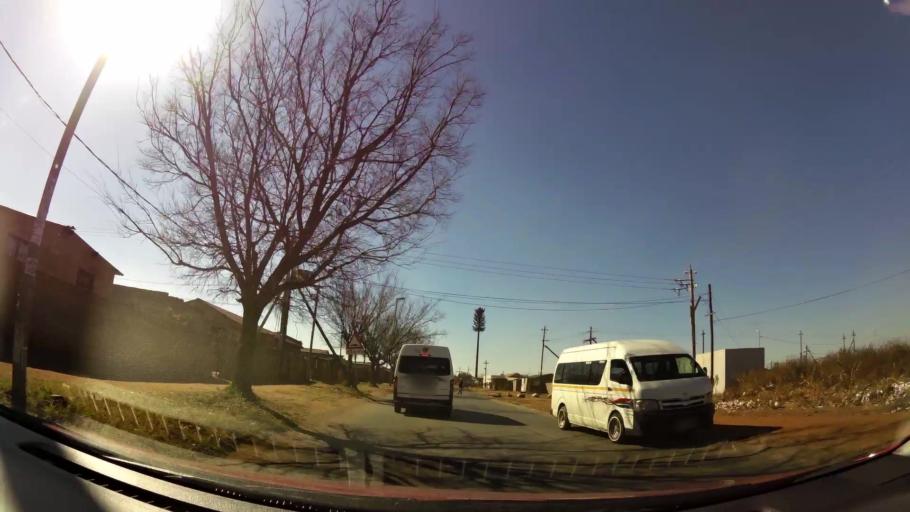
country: ZA
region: Gauteng
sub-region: City of Johannesburg Metropolitan Municipality
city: Soweto
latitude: -26.2250
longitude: 27.8259
